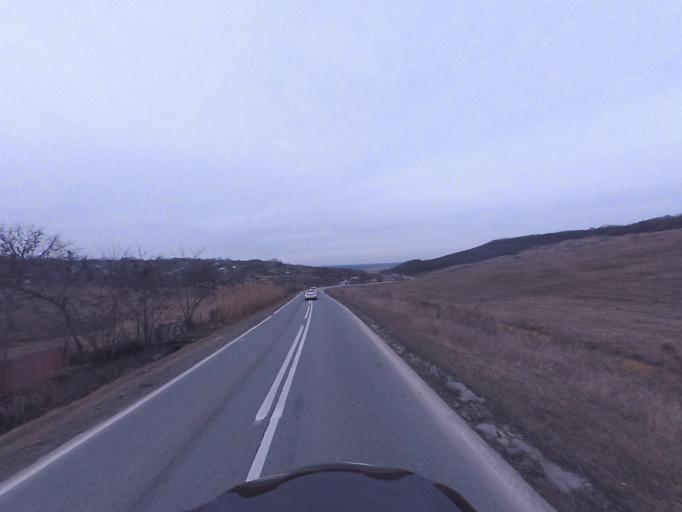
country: RO
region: Iasi
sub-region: Comuna Popricani
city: Popricani
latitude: 47.2938
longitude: 27.5104
